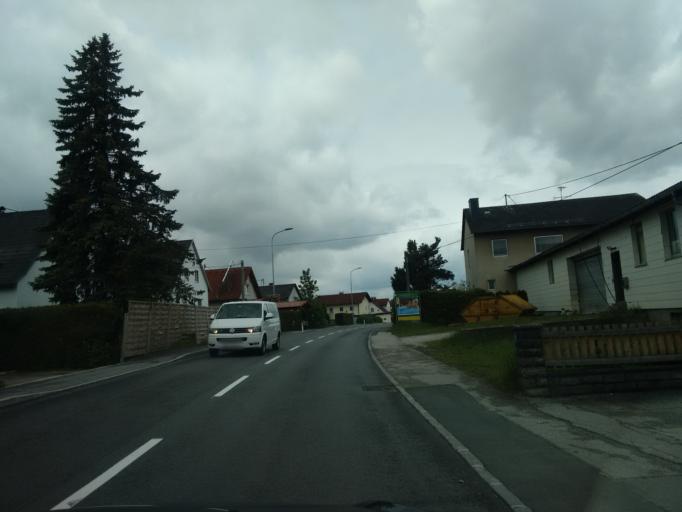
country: AT
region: Upper Austria
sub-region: Politischer Bezirk Steyr-Land
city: Bad Hall
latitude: 48.0247
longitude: 14.2287
